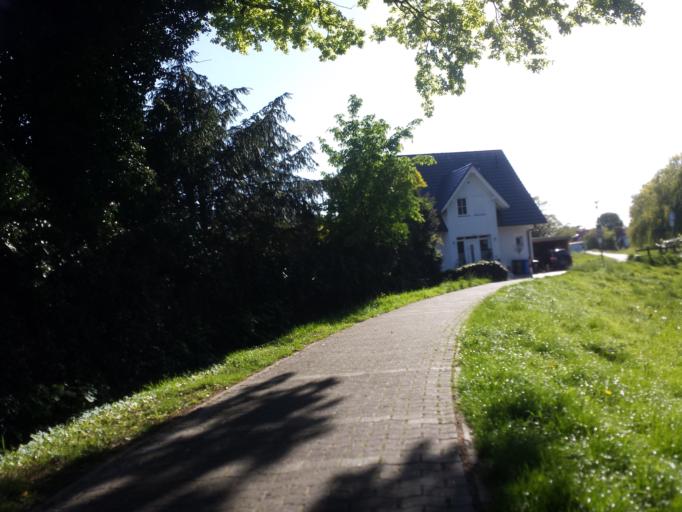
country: DE
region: Lower Saxony
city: Lilienthal
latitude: 53.1395
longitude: 8.9076
